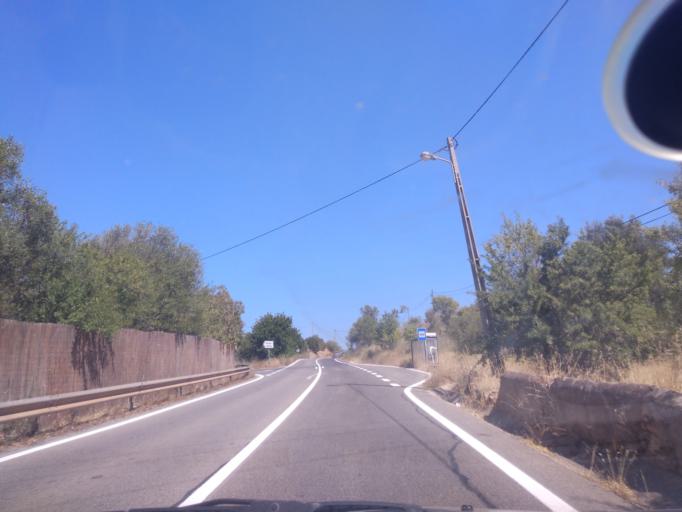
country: PT
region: Faro
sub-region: Lagos
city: Lagos
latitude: 37.1177
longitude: -8.6908
